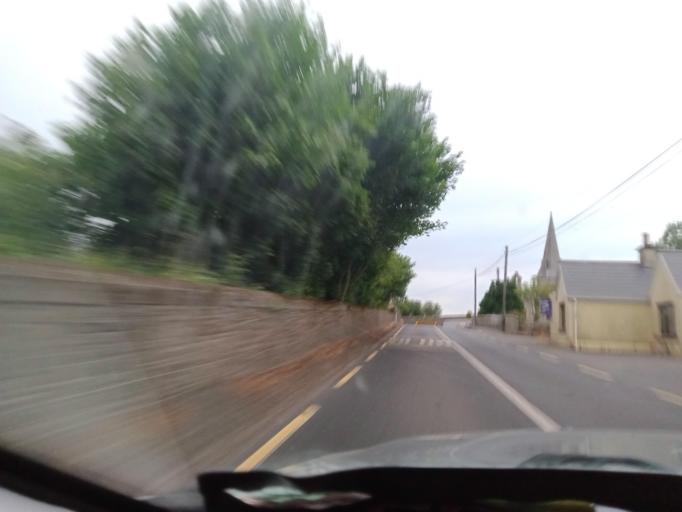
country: IE
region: Leinster
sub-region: Laois
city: Mountmellick
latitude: 53.1352
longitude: -7.4051
